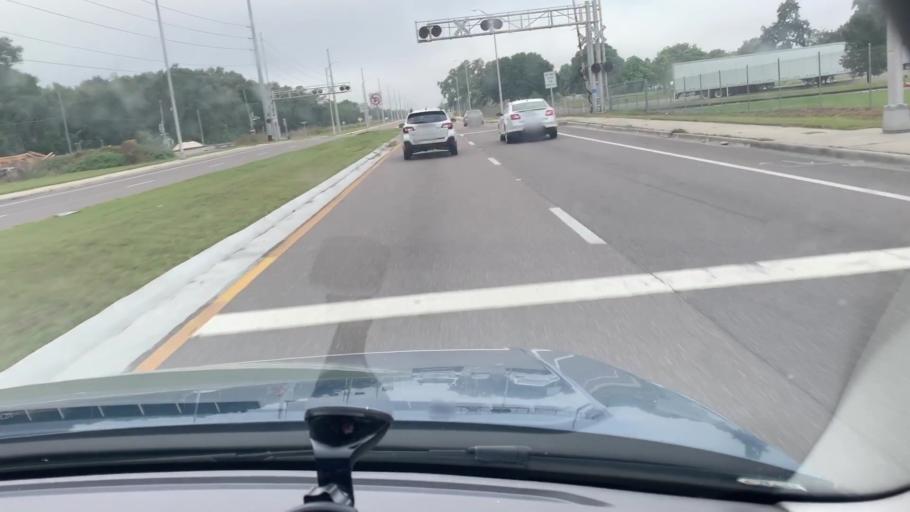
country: US
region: Florida
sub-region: Polk County
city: Kathleen
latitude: 28.1008
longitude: -82.0098
